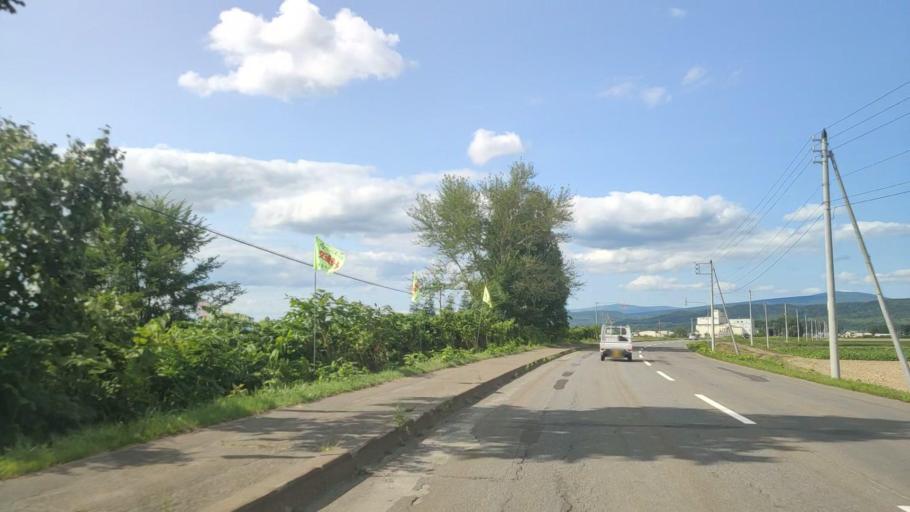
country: JP
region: Hokkaido
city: Nayoro
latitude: 44.4276
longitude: 142.3997
